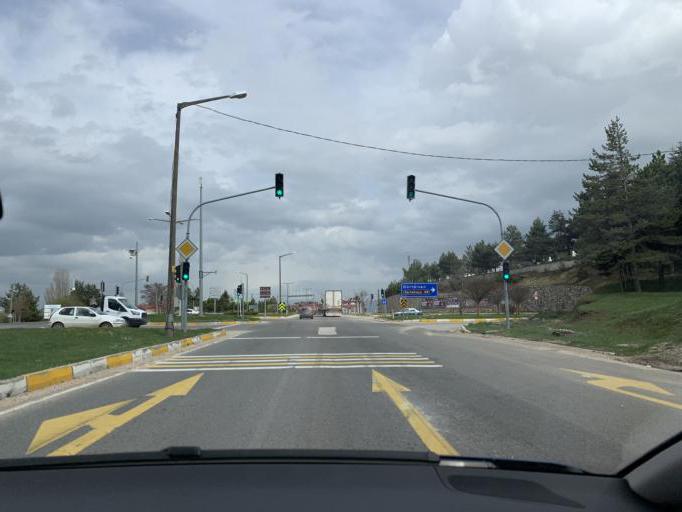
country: TR
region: Bolu
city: Gerede
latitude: 40.7991
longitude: 32.1846
